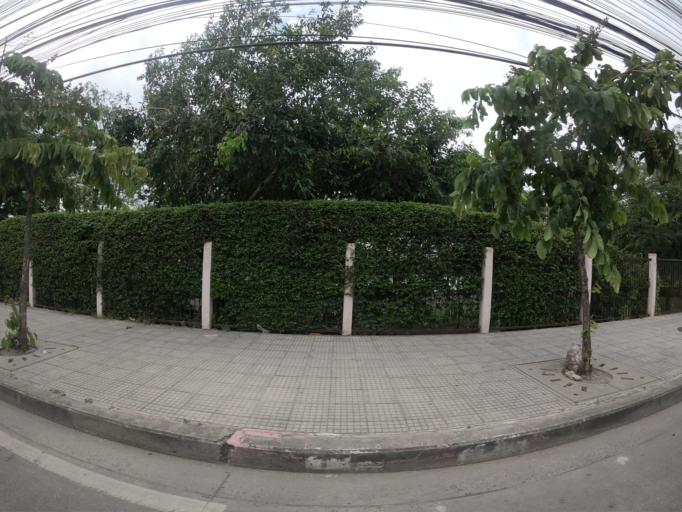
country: TH
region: Bangkok
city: Bang Na
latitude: 13.6753
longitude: 100.6772
